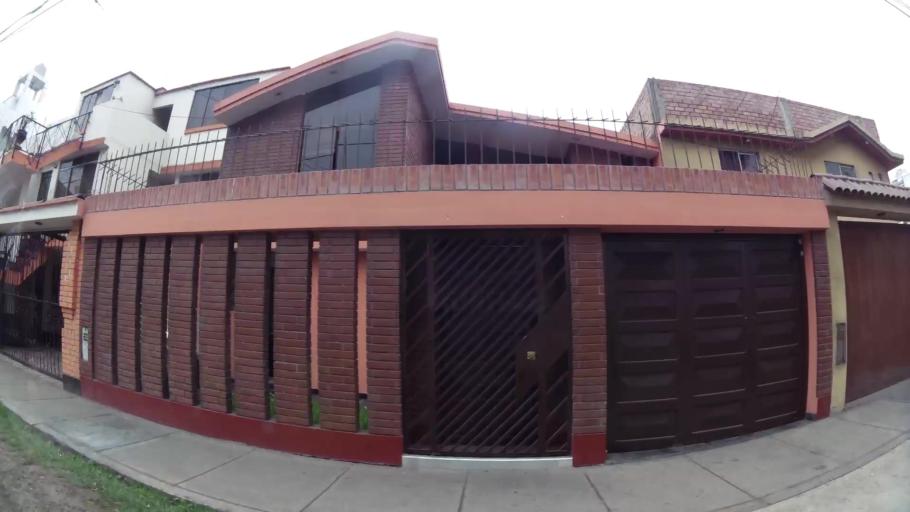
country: PE
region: Lima
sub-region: Lima
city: Surco
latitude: -12.1207
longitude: -77.0051
